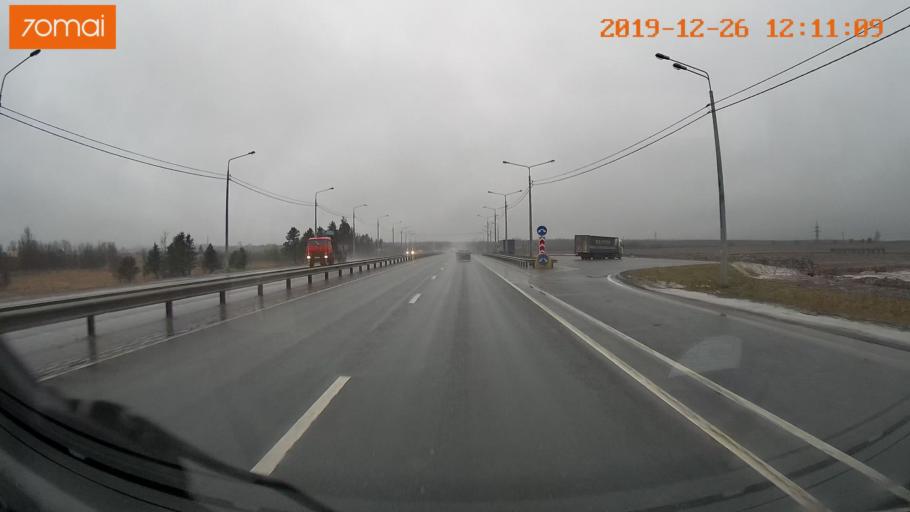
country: RU
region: Vologda
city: Tonshalovo
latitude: 59.2513
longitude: 37.9738
